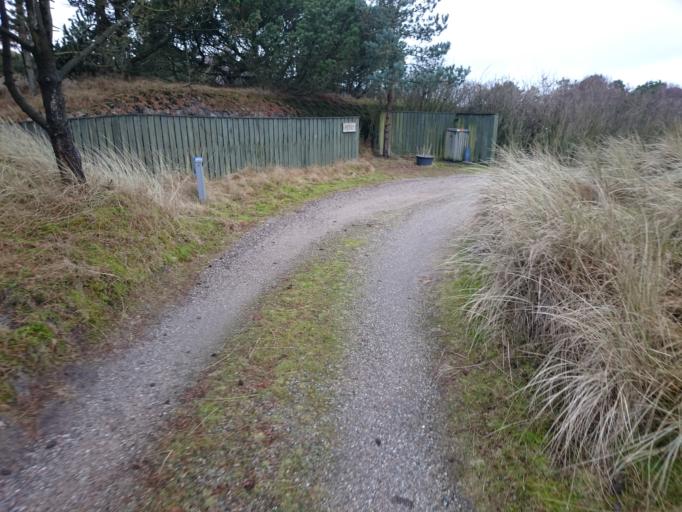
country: DK
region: South Denmark
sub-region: Fano Kommune
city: Nordby
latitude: 55.4337
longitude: 8.3798
